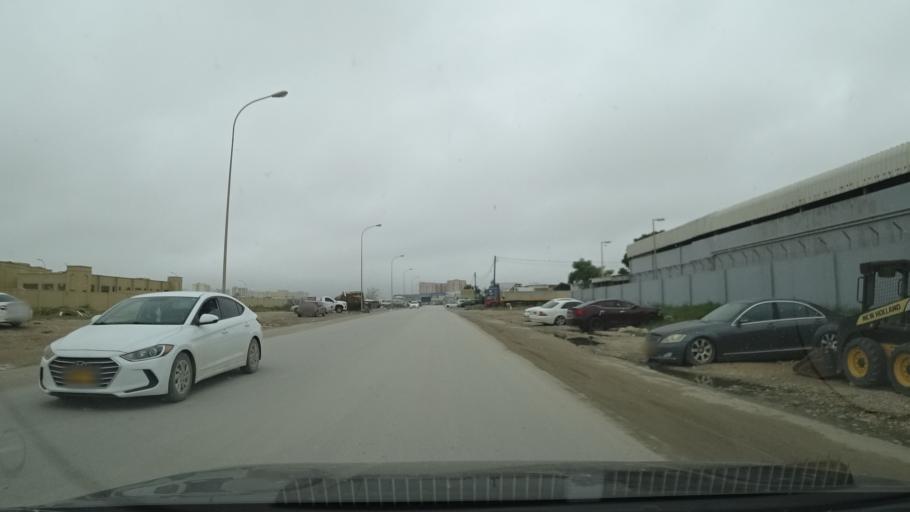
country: OM
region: Zufar
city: Salalah
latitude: 17.0164
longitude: 54.0425
